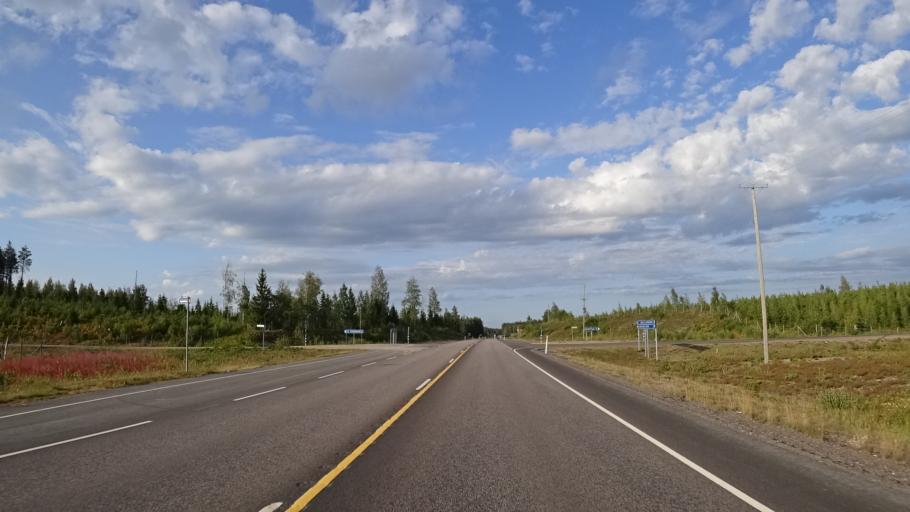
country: FI
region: South Karelia
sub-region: Imatra
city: Rautjaervi
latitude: 61.3908
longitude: 29.2691
